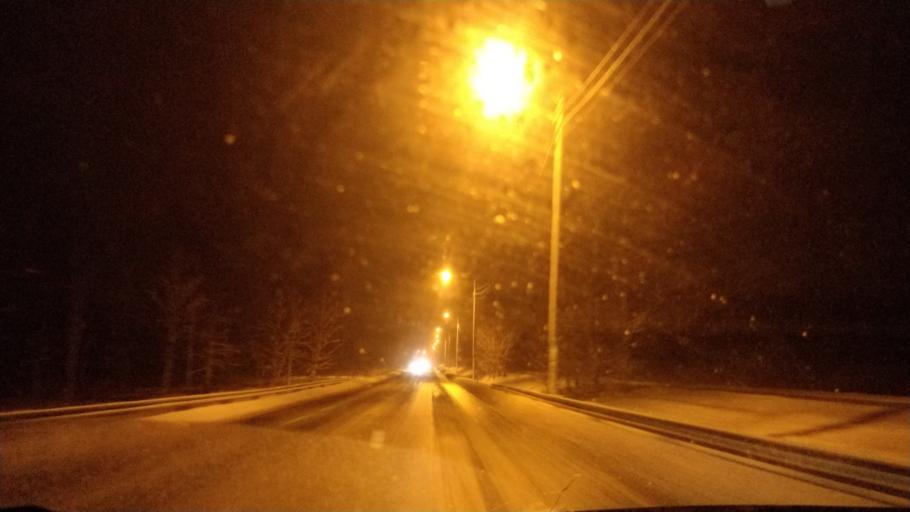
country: FI
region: Lapland
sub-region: Rovaniemi
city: Rovaniemi
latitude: 66.2809
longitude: 25.3361
